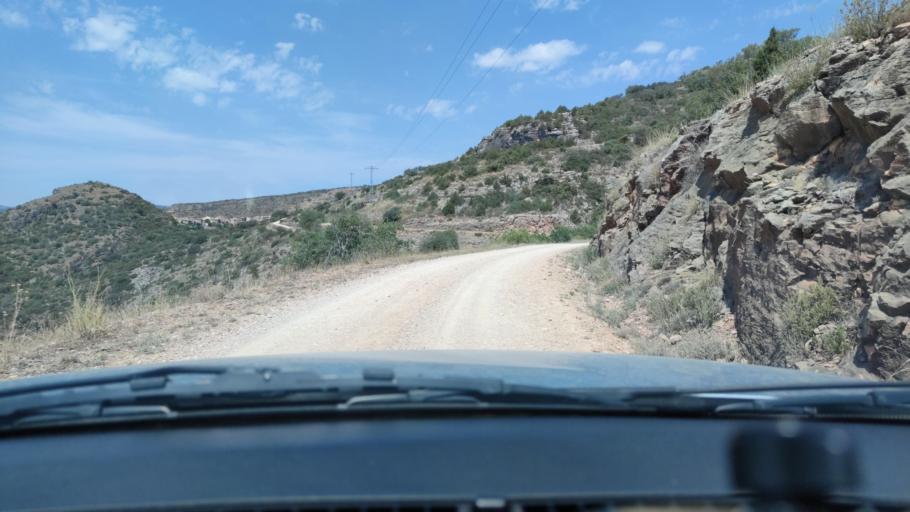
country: ES
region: Catalonia
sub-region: Provincia de Lleida
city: Camarasa
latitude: 41.9268
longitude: 0.8138
